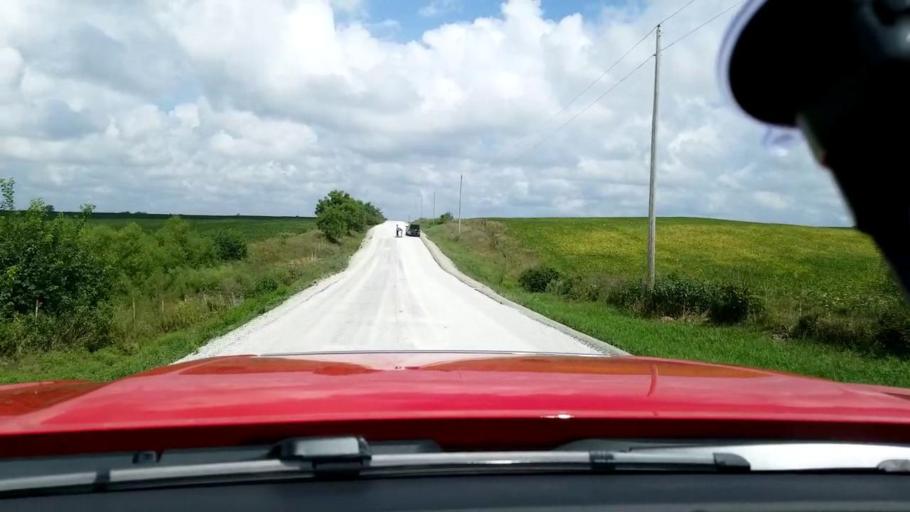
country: US
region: Iowa
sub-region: Decatur County
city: Lamoni
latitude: 40.6628
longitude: -94.0483
